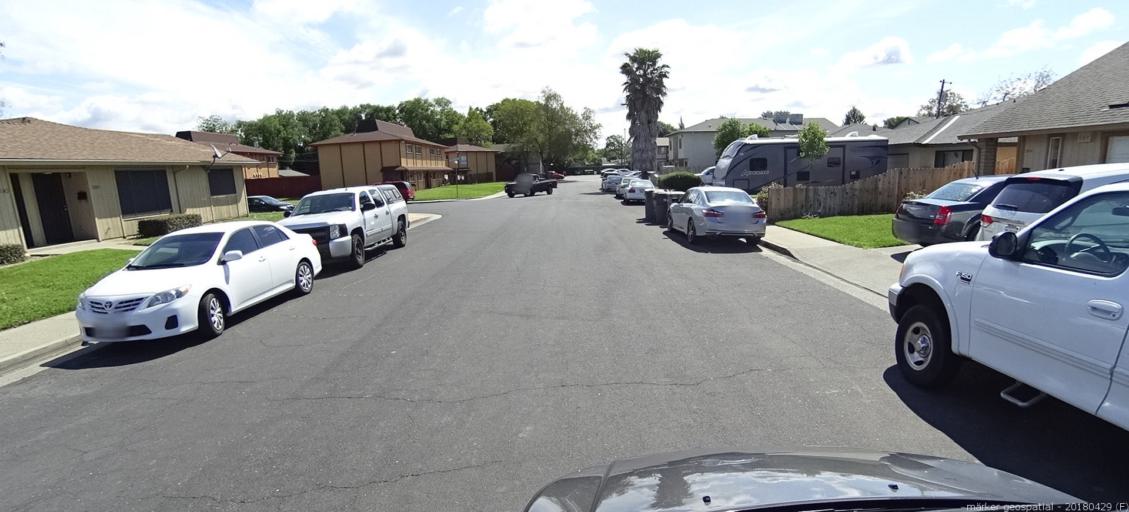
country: US
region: California
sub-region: Yolo County
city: West Sacramento
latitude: 38.5763
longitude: -121.5390
